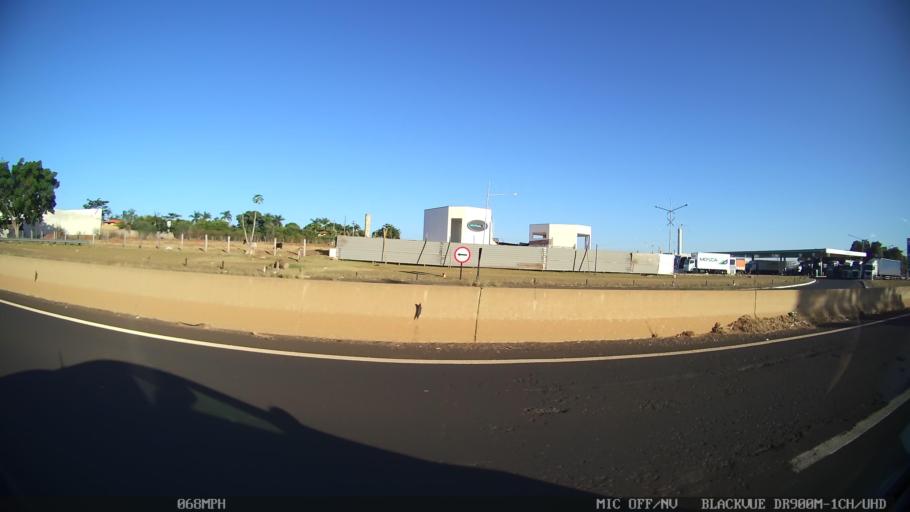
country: BR
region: Sao Paulo
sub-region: Guapiacu
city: Guapiacu
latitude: -20.7896
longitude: -49.2926
